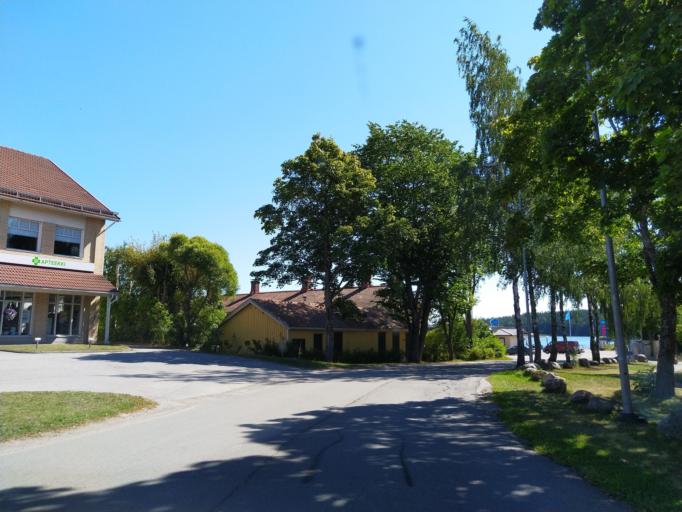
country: FI
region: Varsinais-Suomi
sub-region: Aboland-Turunmaa
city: Dragsfjaerd
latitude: 60.0201
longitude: 22.5091
